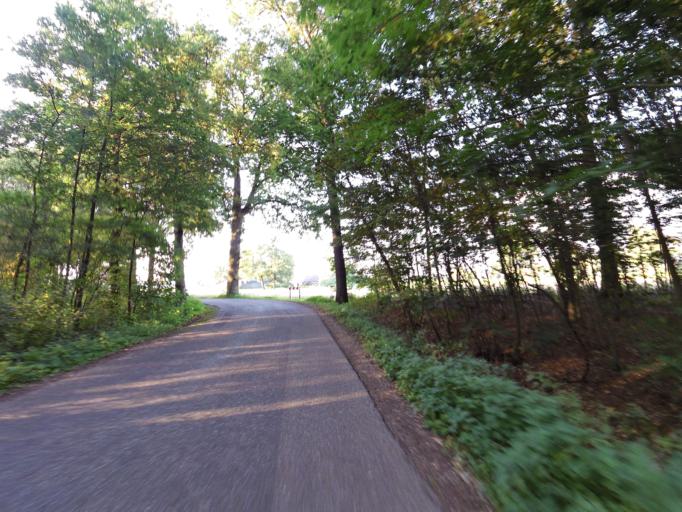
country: NL
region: Gelderland
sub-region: Oude IJsselstreek
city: Wisch
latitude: 51.9376
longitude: 6.3888
